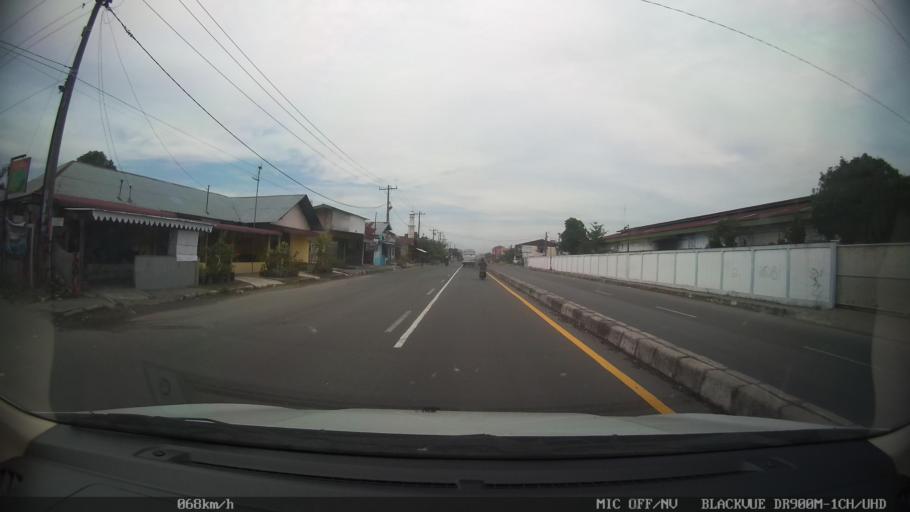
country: ID
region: North Sumatra
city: Sunggal
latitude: 3.6101
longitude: 98.5757
